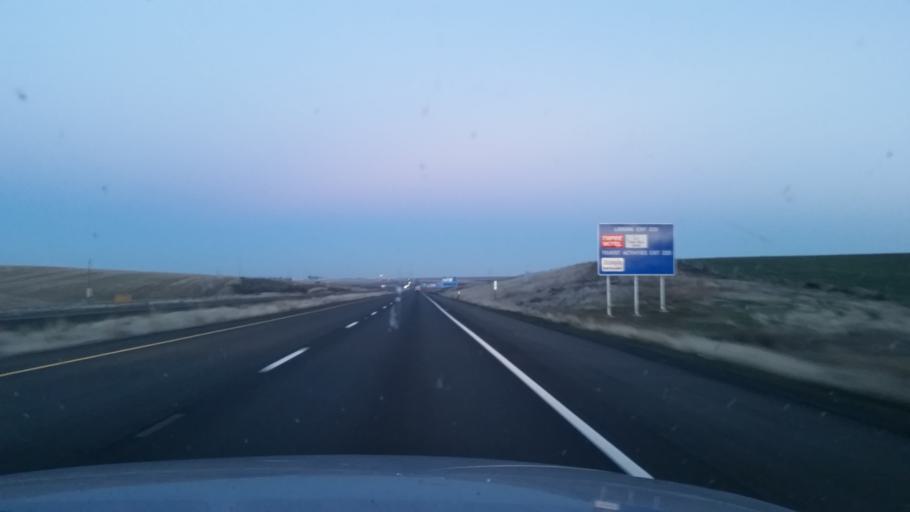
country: US
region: Washington
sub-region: Adams County
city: Ritzville
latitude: 47.1109
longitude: -118.4284
